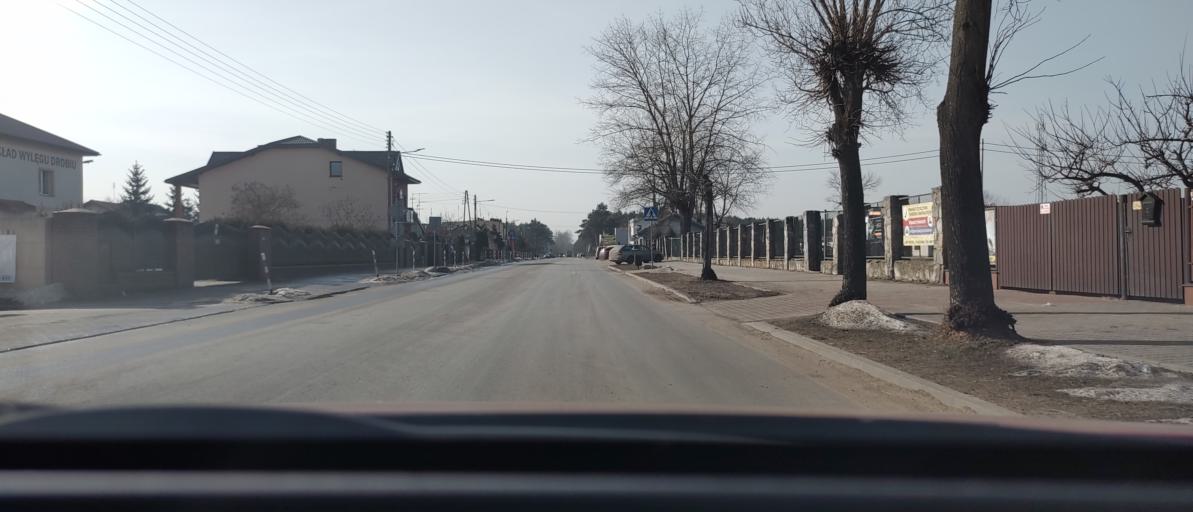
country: PL
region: Masovian Voivodeship
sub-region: Powiat bialobrzeski
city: Bialobrzegi
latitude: 51.6476
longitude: 20.9419
